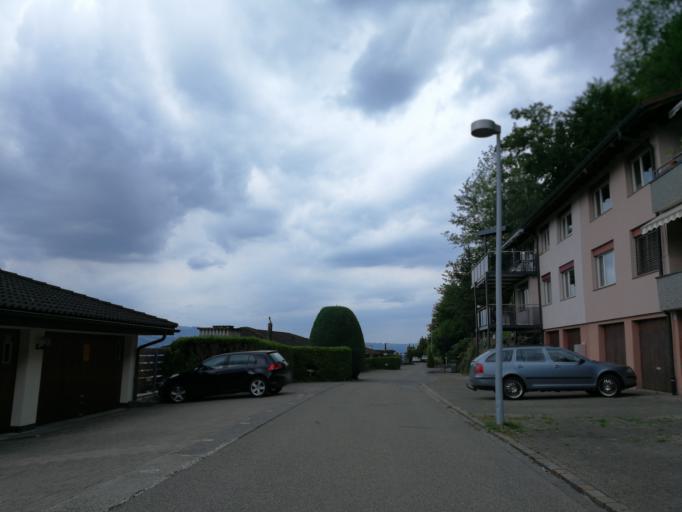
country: CH
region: Saint Gallen
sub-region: Wahlkreis See-Gaster
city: Jona
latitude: 47.2321
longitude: 8.8540
